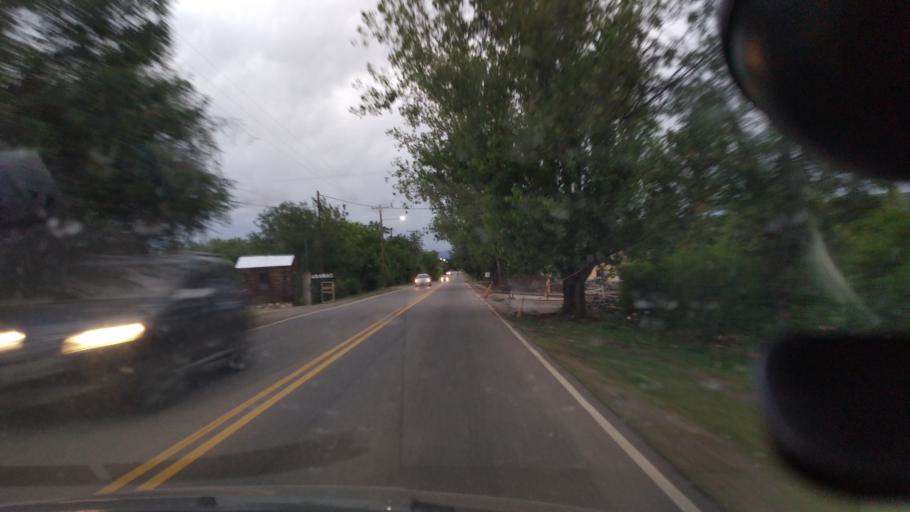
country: AR
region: Cordoba
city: Villa Las Rosas
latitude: -31.9167
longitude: -65.0375
